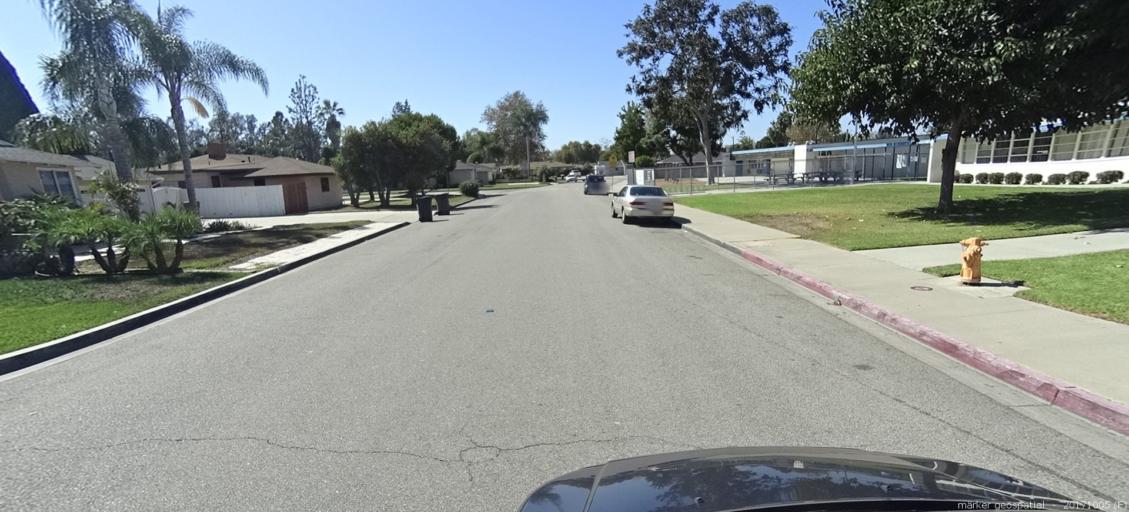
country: US
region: California
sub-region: Orange County
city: Garden Grove
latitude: 33.7835
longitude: -117.9611
